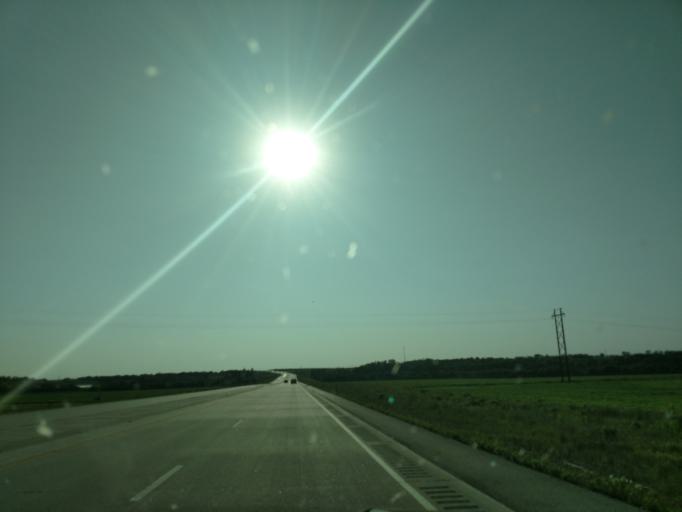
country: US
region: Nebraska
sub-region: Sarpy County
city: Offutt Air Force Base
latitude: 41.0800
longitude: -95.9073
